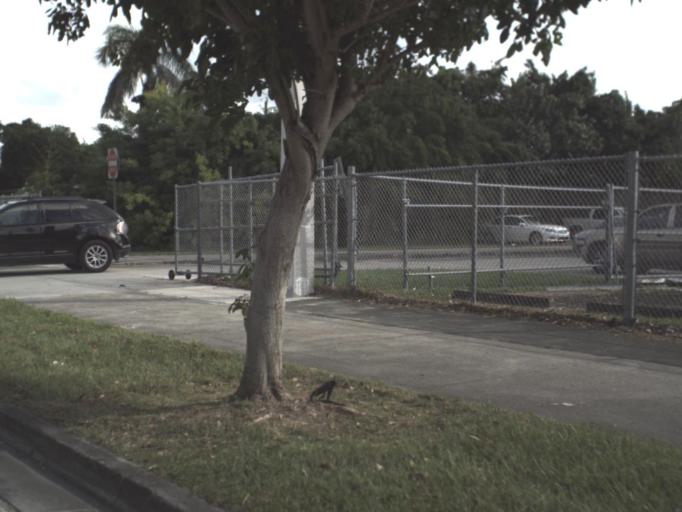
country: US
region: Florida
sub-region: Miami-Dade County
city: Leisure City
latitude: 25.4994
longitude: -80.4323
